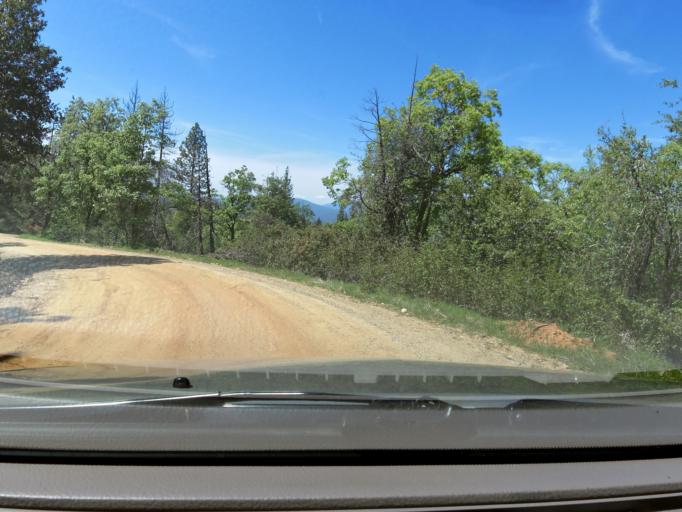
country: US
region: California
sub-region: Madera County
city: Oakhurst
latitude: 37.2855
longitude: -119.6234
